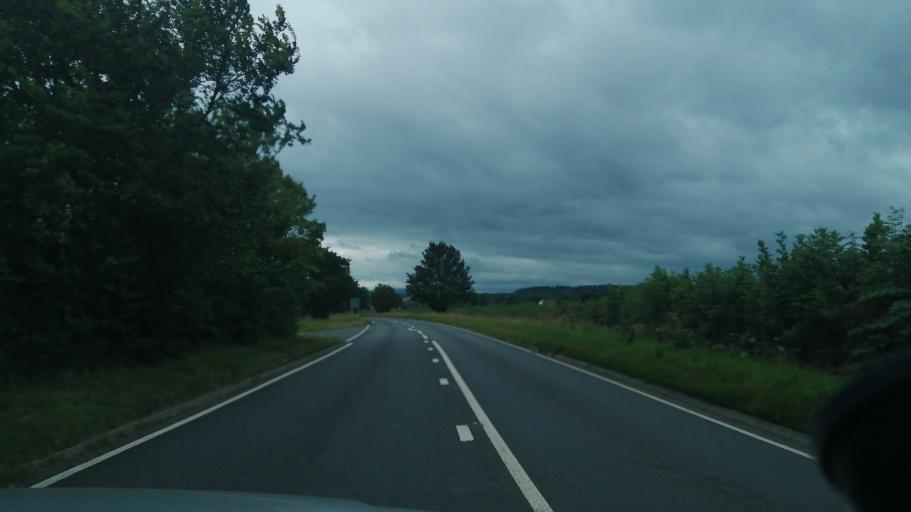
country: GB
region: England
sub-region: Herefordshire
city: Thruxton
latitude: 52.0049
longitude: -2.7917
